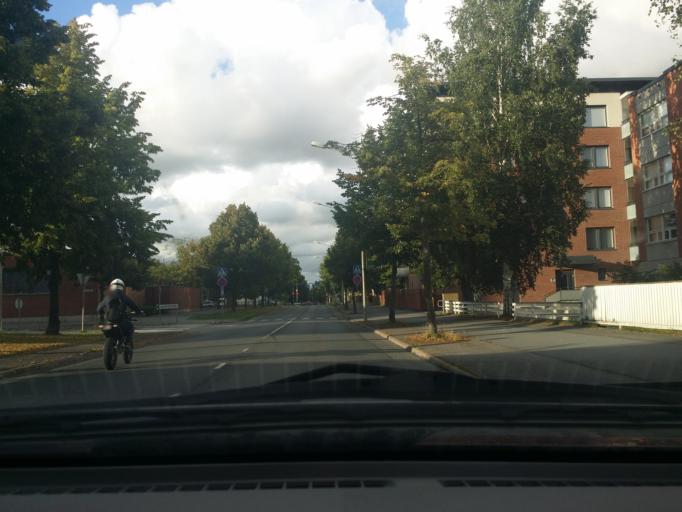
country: FI
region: Satakunta
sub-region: Pori
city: Pori
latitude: 61.4856
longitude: 21.8018
